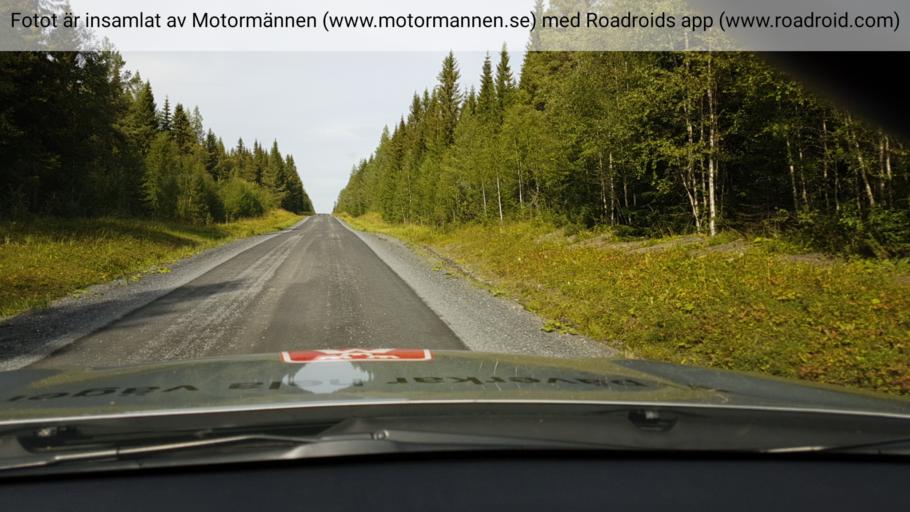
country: SE
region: Jaemtland
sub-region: Krokoms Kommun
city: Valla
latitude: 63.3331
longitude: 13.8393
